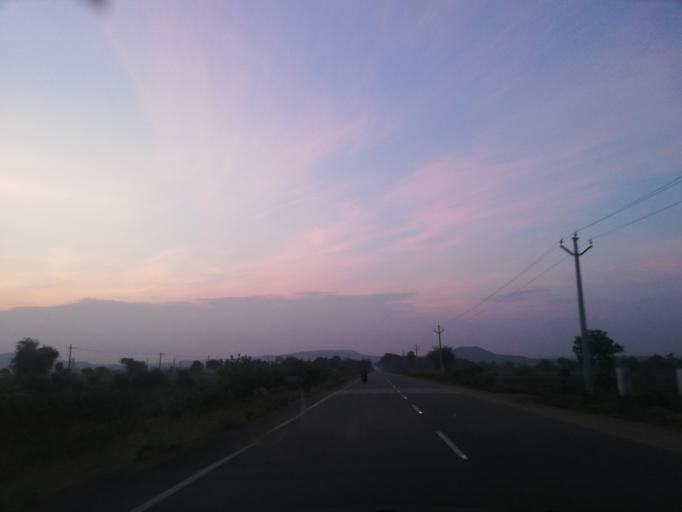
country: IN
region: Andhra Pradesh
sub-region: Guntur
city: Macherla
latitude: 16.6858
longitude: 79.2544
